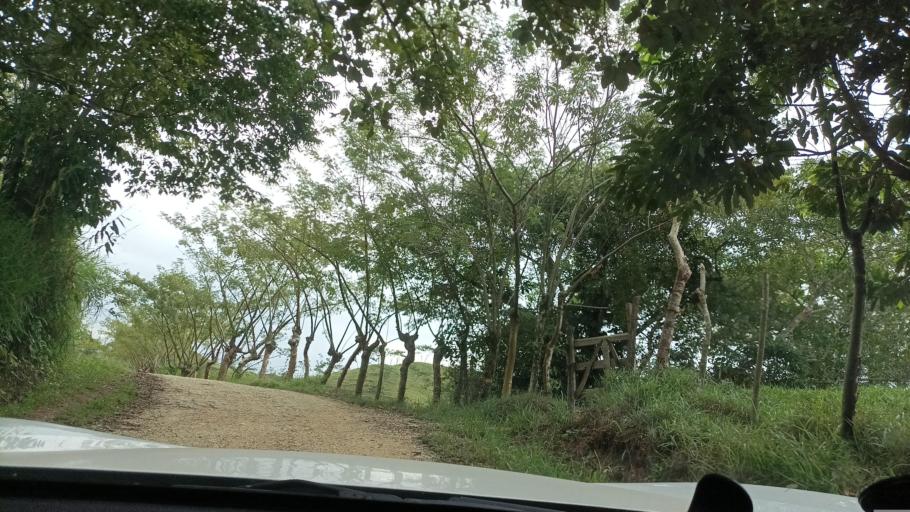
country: MX
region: Veracruz
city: Hidalgotitlan
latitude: 17.5983
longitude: -94.4223
